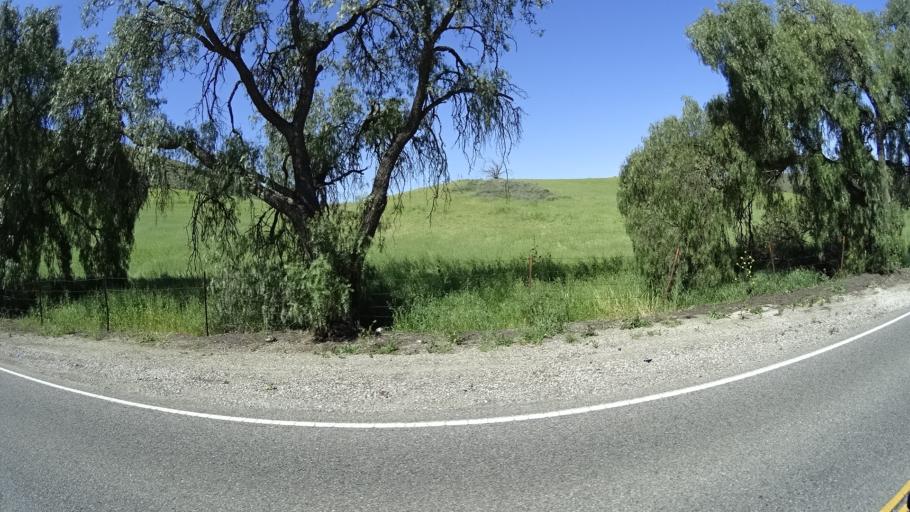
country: US
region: California
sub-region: Ventura County
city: Moorpark
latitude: 34.2404
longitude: -118.8629
